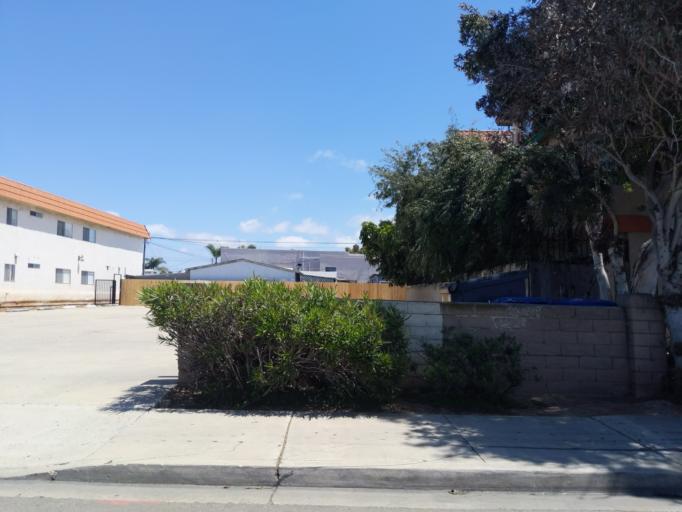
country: US
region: California
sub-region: San Diego County
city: Imperial Beach
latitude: 32.5826
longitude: -117.1142
